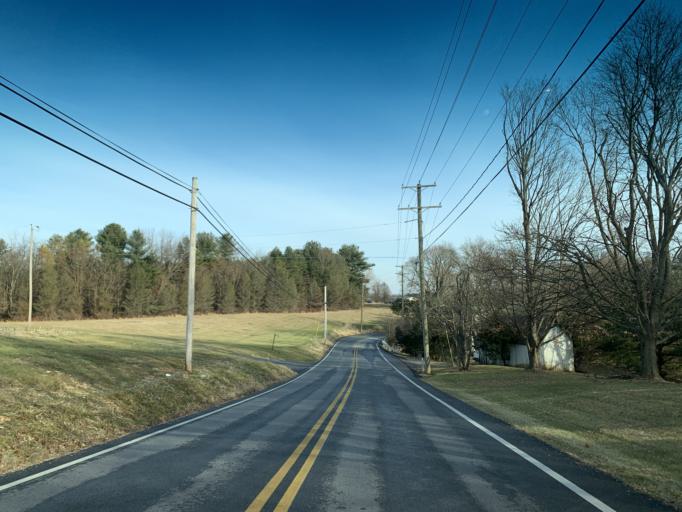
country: US
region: Maryland
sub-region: Carroll County
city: Hampstead
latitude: 39.6135
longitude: -76.8041
